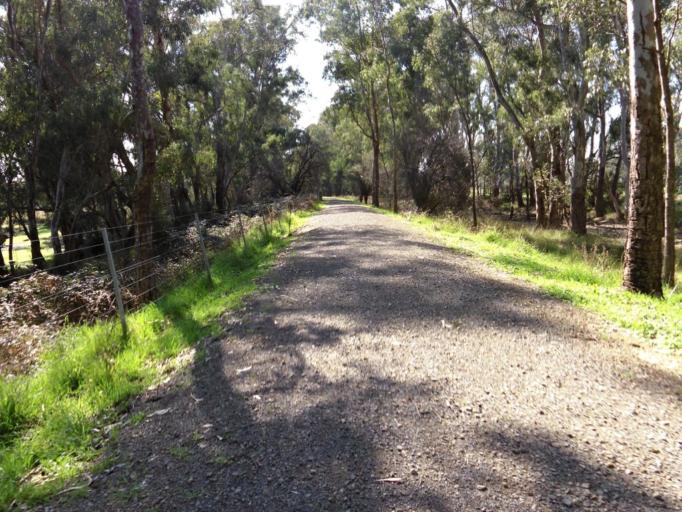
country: AU
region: Victoria
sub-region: Murrindindi
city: Alexandra
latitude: -37.1570
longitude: 145.5719
